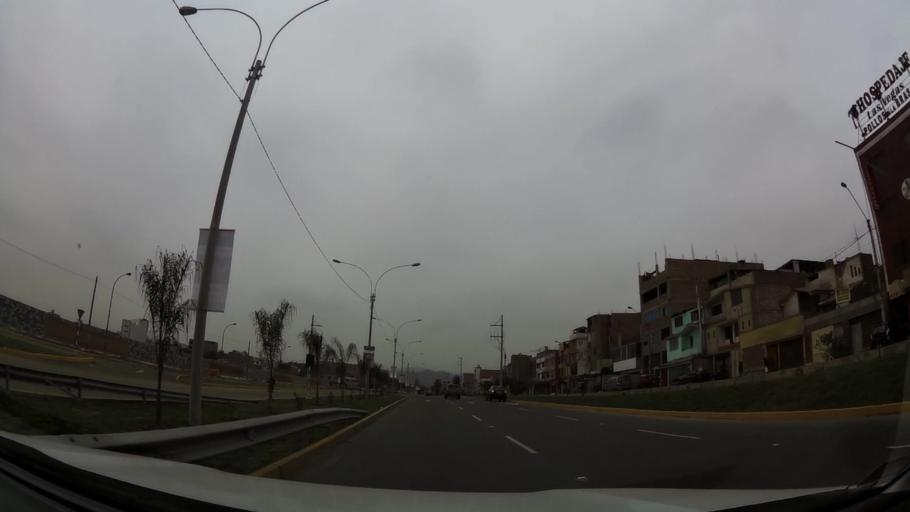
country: PE
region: Lima
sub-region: Lima
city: Vitarte
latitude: -12.0439
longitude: -76.9321
